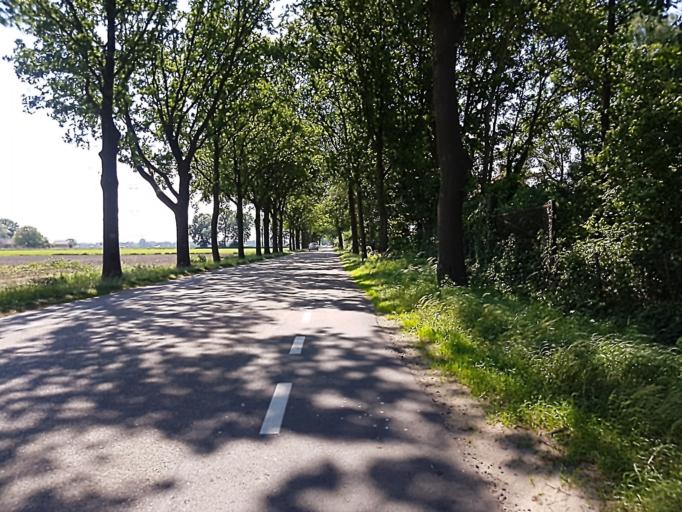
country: NL
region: North Brabant
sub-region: Gemeente Dongen
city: Dongen
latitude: 51.6375
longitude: 4.9935
